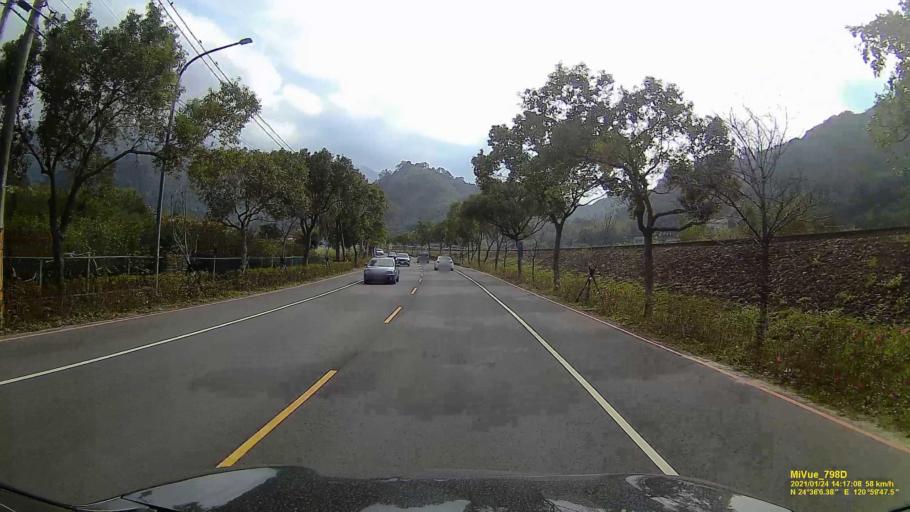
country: TW
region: Taiwan
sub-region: Miaoli
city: Miaoli
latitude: 24.6015
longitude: 120.9965
